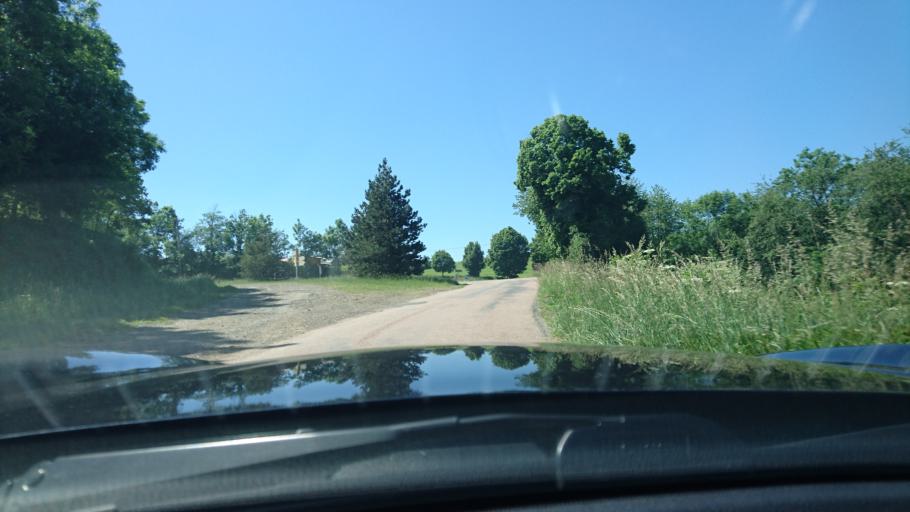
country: FR
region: Rhone-Alpes
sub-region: Departement de la Loire
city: Bussieres
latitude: 45.8449
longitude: 4.2651
